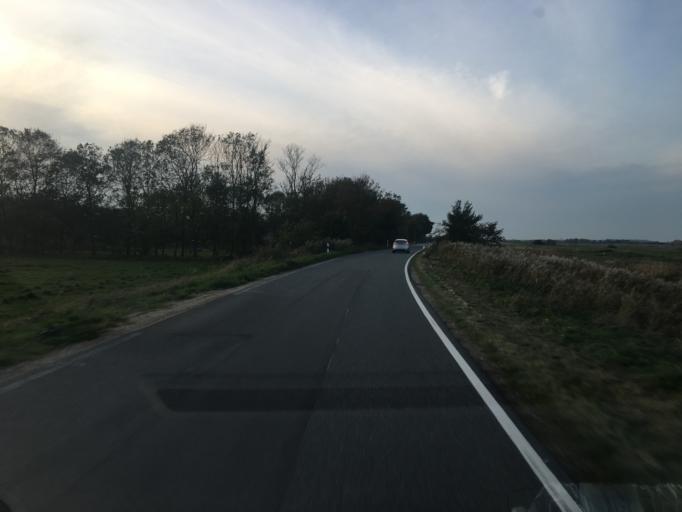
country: DE
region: Schleswig-Holstein
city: Aventoft
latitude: 54.8987
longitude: 8.8456
